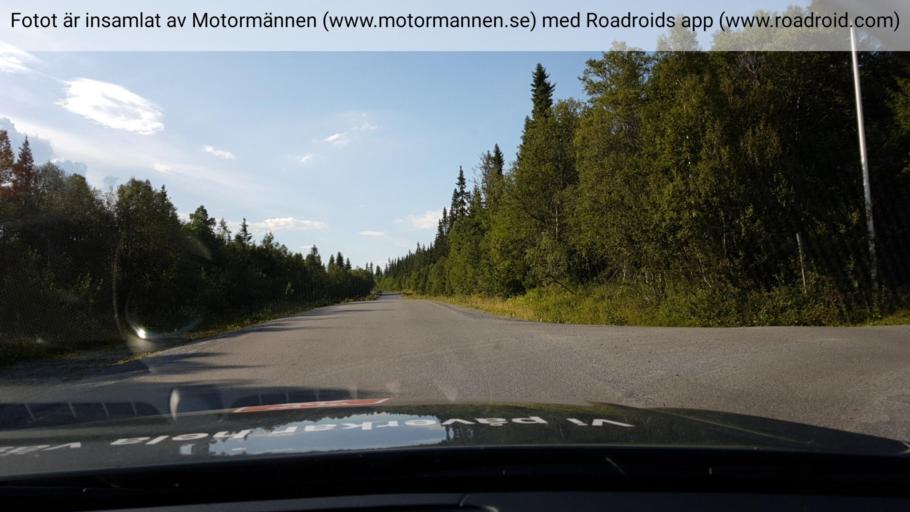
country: SE
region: Jaemtland
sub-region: Are Kommun
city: Are
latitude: 63.4147
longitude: 13.0277
